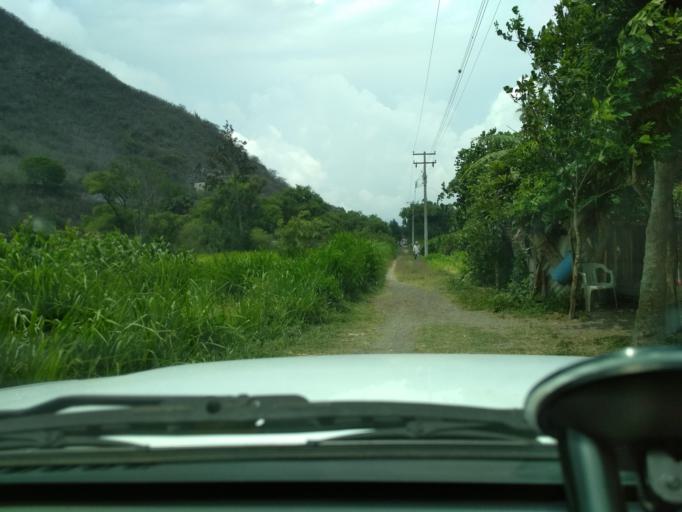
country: MX
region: Veracruz
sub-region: Nogales
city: Taza de Agua Ojo Zarco
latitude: 18.7815
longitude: -97.2137
